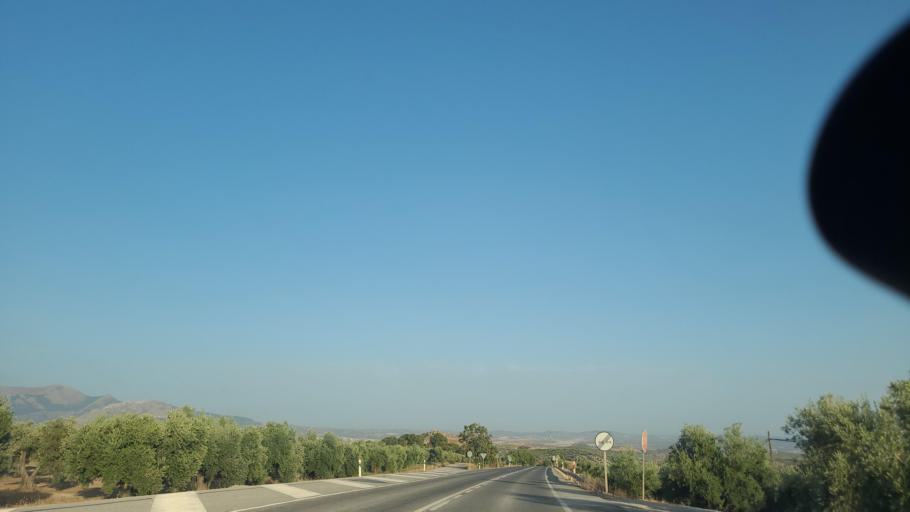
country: ES
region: Andalusia
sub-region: Provincia de Jaen
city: Mancha Real
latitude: 37.8031
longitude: -3.6425
